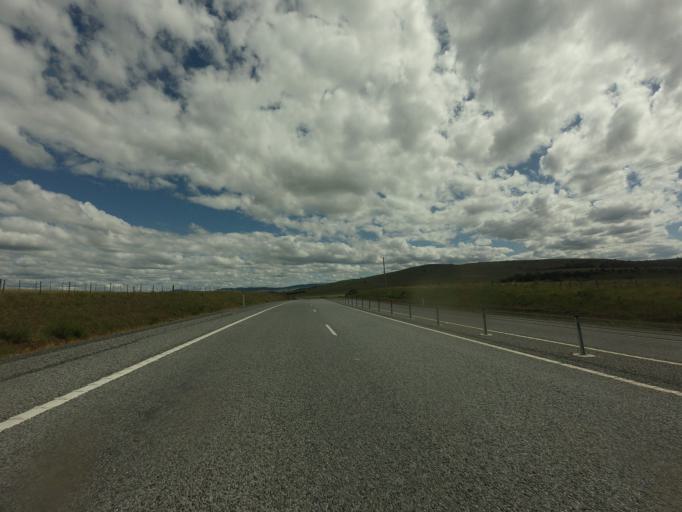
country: AU
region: Tasmania
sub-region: Northern Midlands
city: Evandale
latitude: -42.1000
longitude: 147.4520
